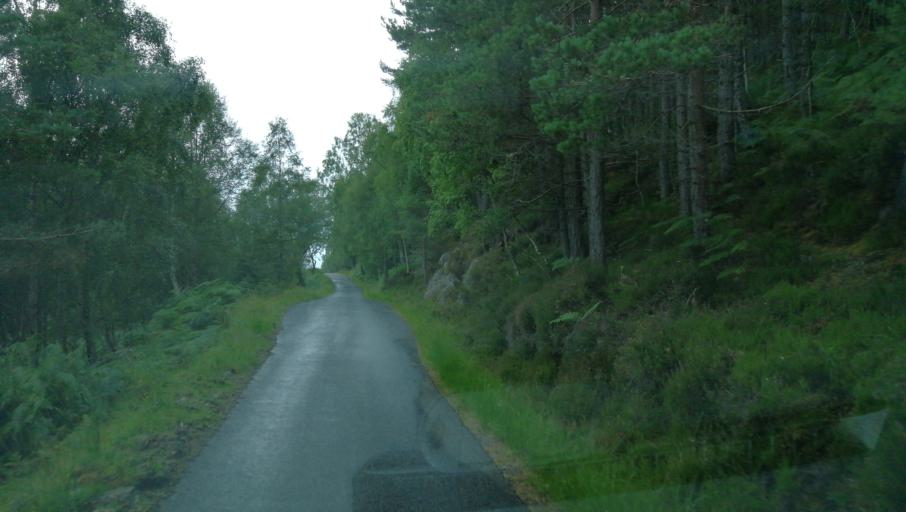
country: GB
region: Scotland
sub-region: Highland
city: Spean Bridge
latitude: 57.2802
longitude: -4.9366
